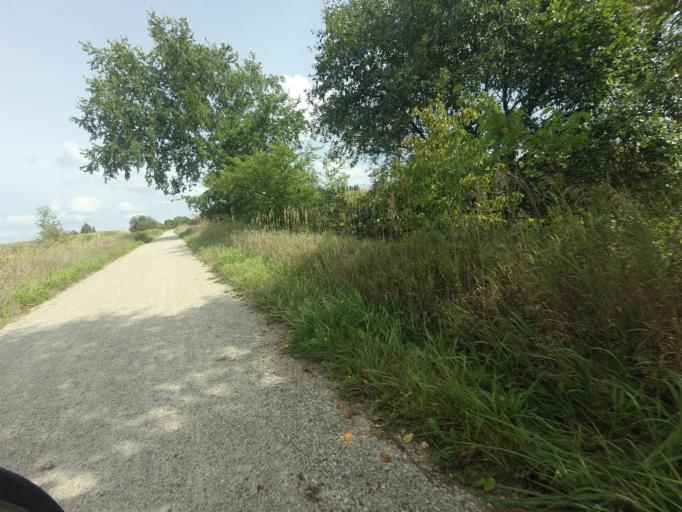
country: CA
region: Ontario
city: Waterloo
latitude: 43.5957
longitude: -80.4845
